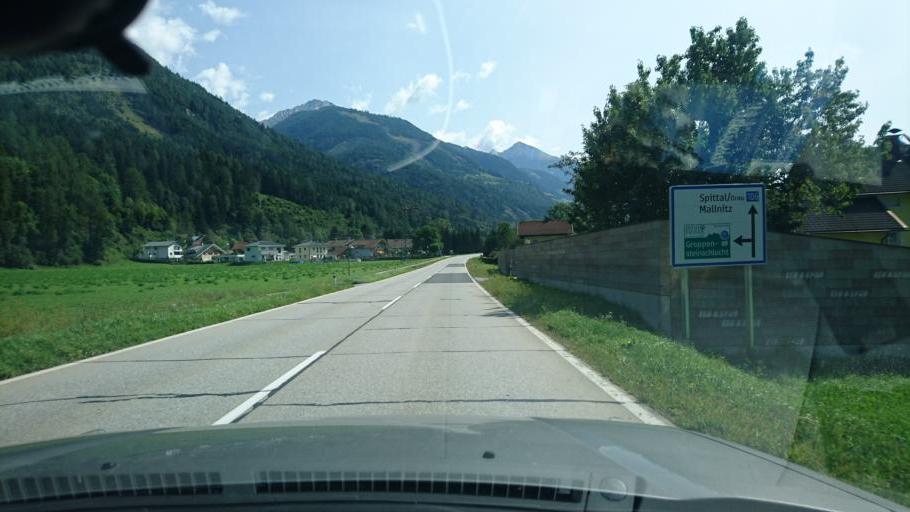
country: AT
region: Carinthia
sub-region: Politischer Bezirk Spittal an der Drau
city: Obervellach
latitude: 46.9390
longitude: 13.1788
